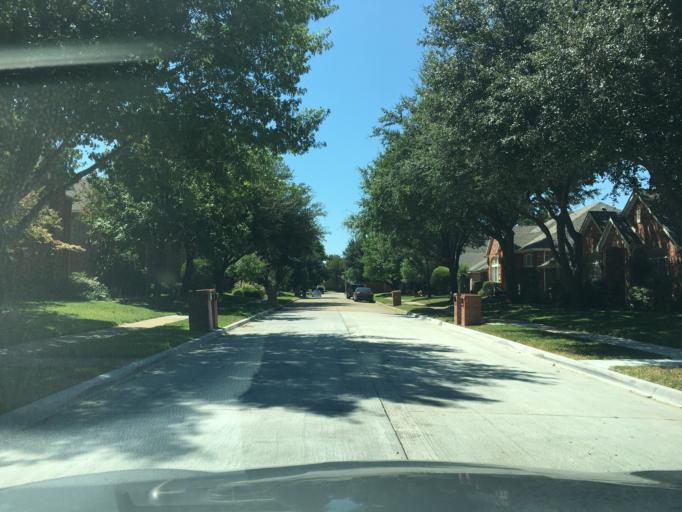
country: US
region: Texas
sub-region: Dallas County
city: Sachse
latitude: 32.9662
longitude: -96.6326
